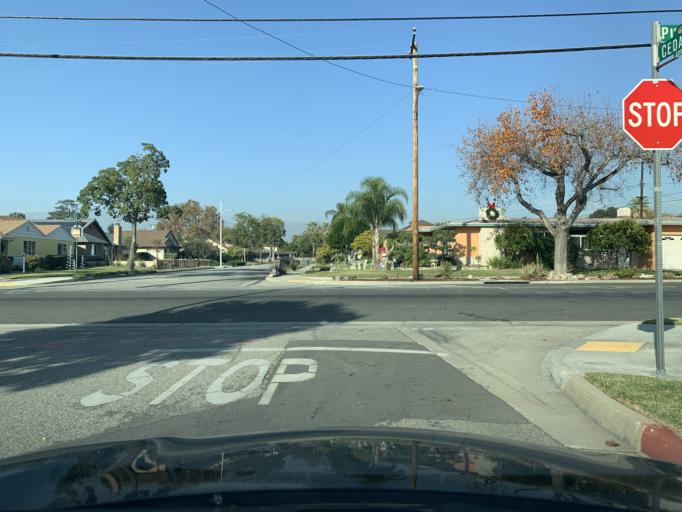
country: US
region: California
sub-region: Los Angeles County
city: Covina
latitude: 34.0825
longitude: -117.8979
